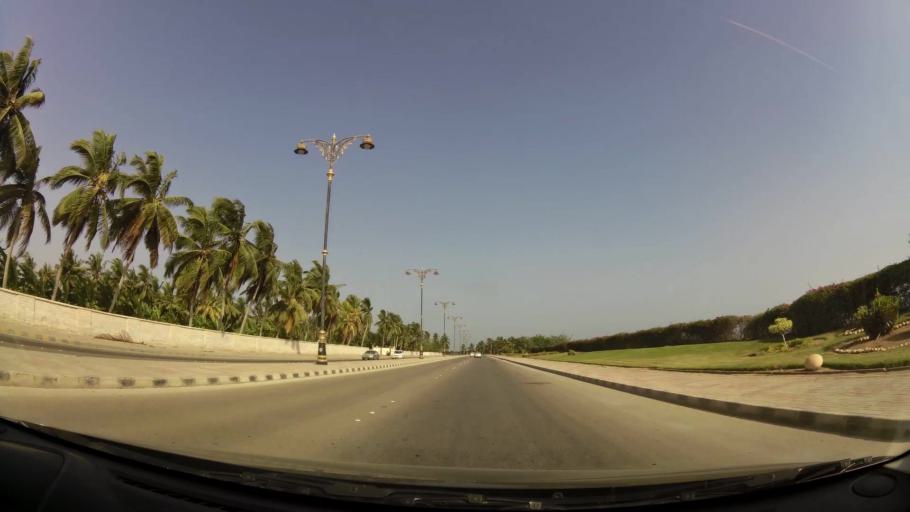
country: OM
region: Zufar
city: Salalah
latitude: 17.0010
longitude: 54.0688
